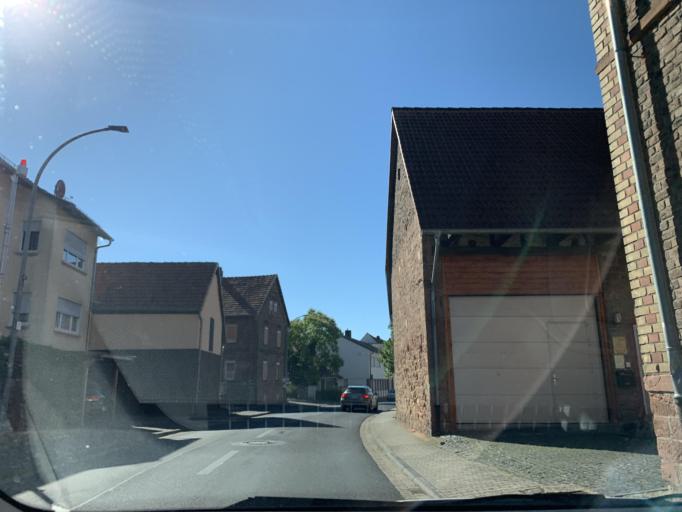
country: DE
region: Hesse
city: Hain-Grundau
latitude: 50.2095
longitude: 9.1399
